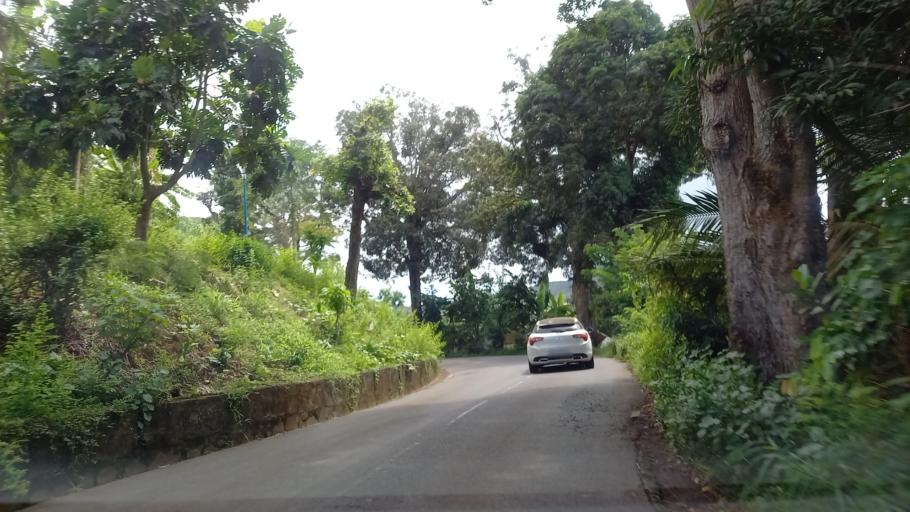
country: YT
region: Mamoudzou
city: Mamoudzou
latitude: -12.7896
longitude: 45.1782
